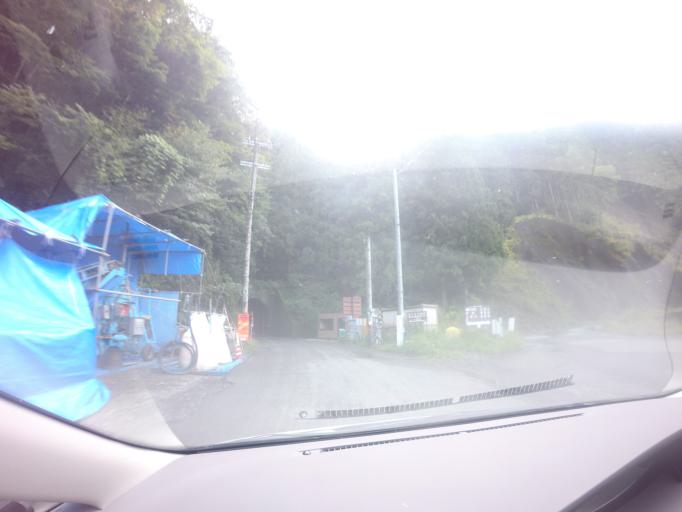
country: JP
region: Wakayama
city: Shingu
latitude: 33.9617
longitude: 135.8524
